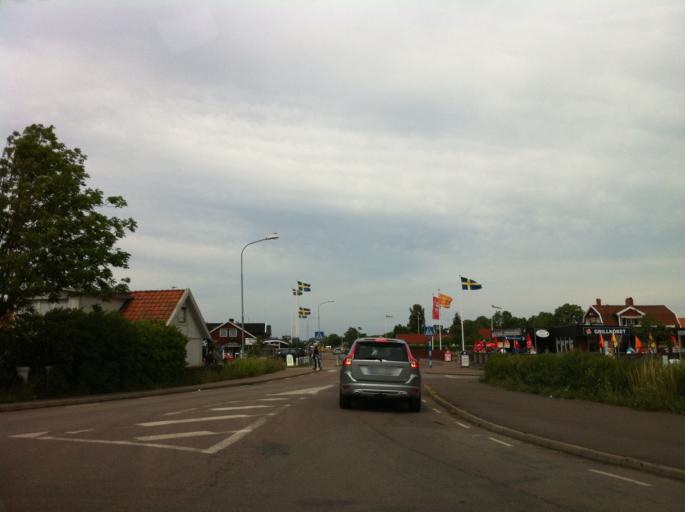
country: SE
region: Kalmar
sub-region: Oskarshamns Kommun
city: Oskarshamn
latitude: 57.3246
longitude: 17.0082
